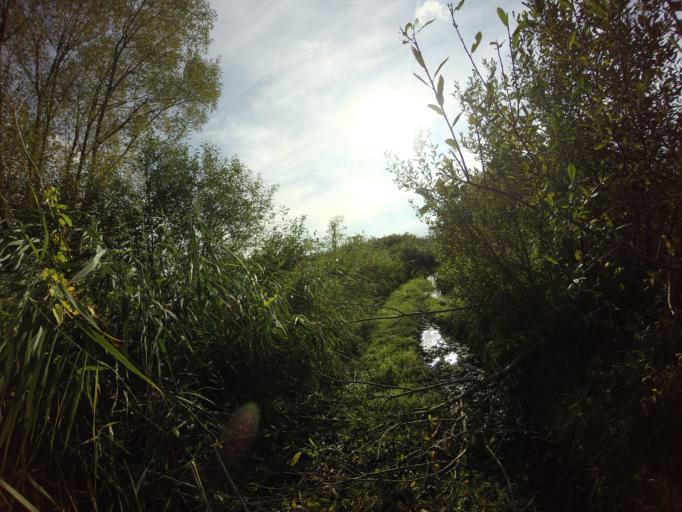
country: PL
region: West Pomeranian Voivodeship
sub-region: Powiat choszczenski
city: Choszczno
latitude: 53.1743
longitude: 15.4046
